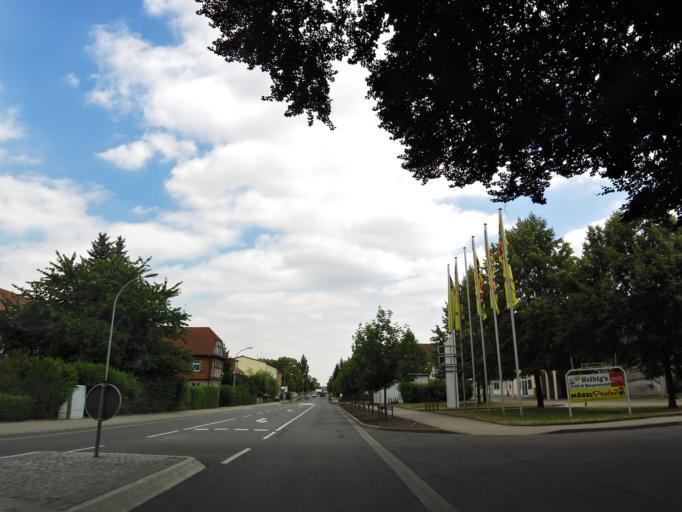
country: DE
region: Thuringia
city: Bad Langensalza
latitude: 51.1061
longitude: 10.6562
